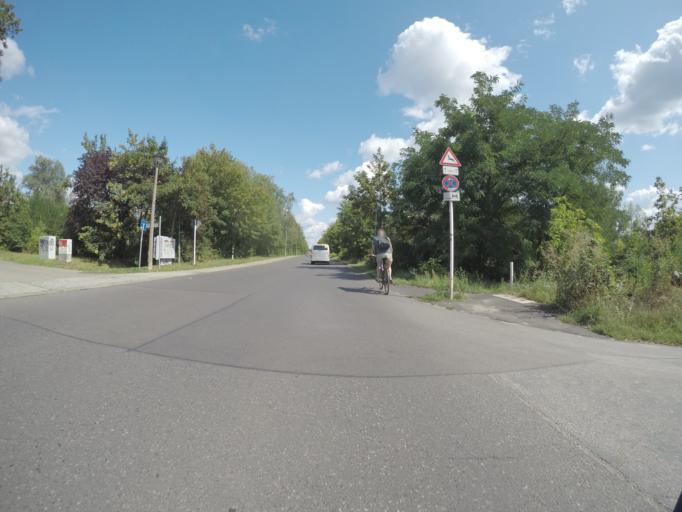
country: DE
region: Berlin
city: Kaulsdorf
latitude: 52.5027
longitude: 13.5883
